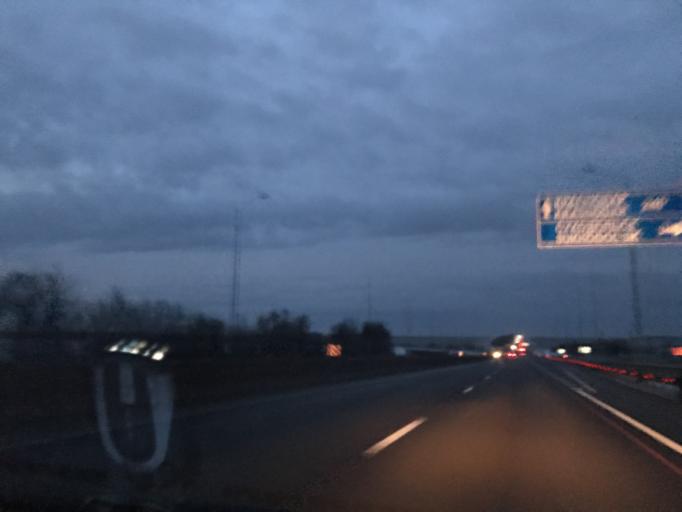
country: RU
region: Rostov
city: Samarskoye
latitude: 47.0060
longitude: 39.7317
